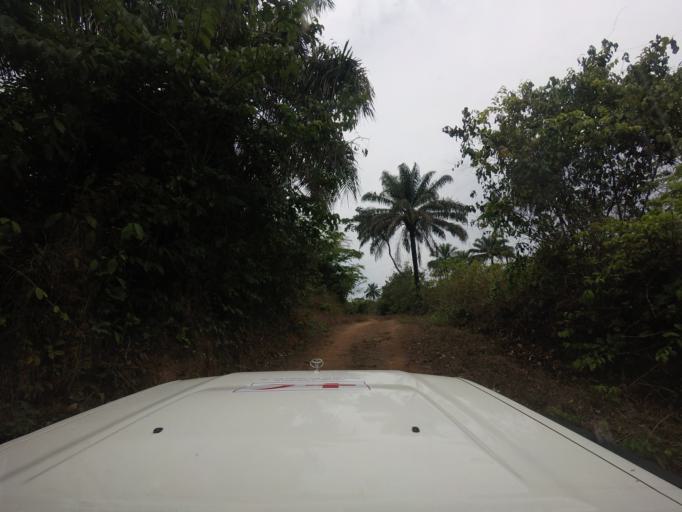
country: SL
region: Eastern Province
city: Buedu
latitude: 8.2388
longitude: -10.2930
